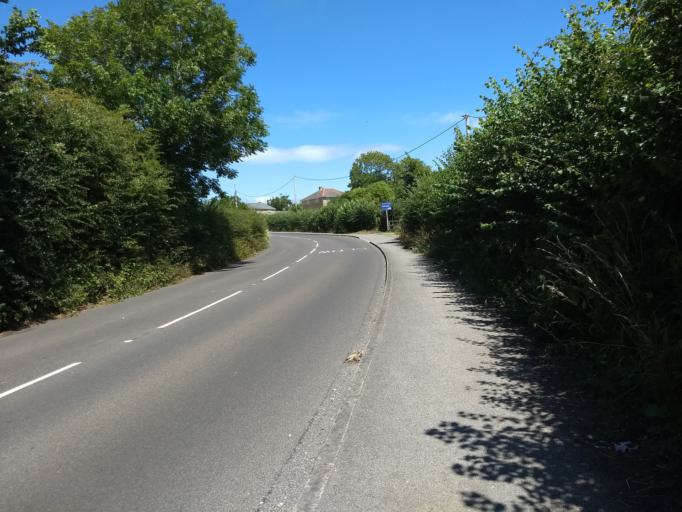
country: GB
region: England
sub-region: Isle of Wight
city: Seaview
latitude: 50.6936
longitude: -1.1201
